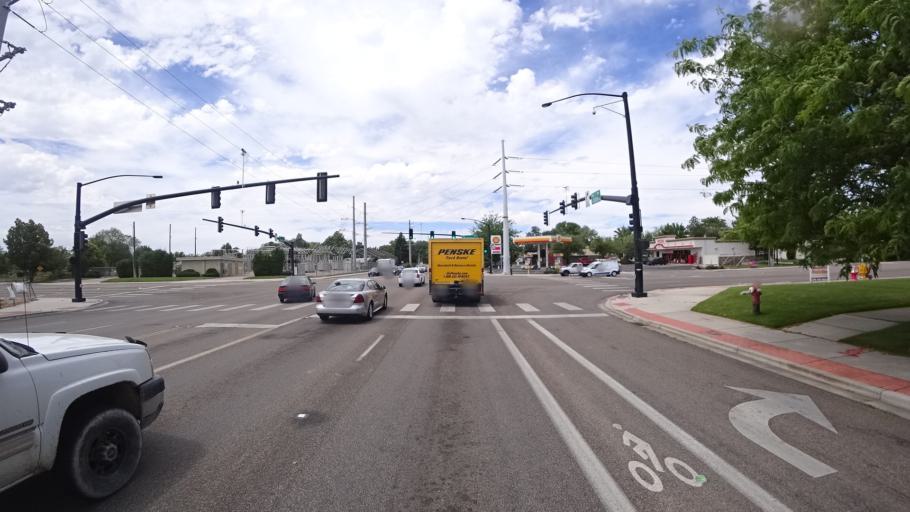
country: US
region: Idaho
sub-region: Ada County
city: Garden City
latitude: 43.6340
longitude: -116.2937
